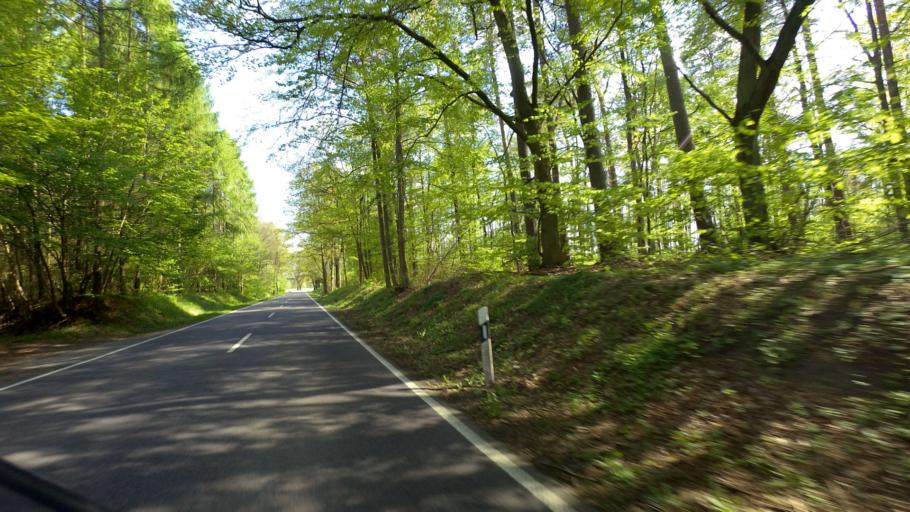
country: DE
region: Brandenburg
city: Templin
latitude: 53.0643
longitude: 13.5167
